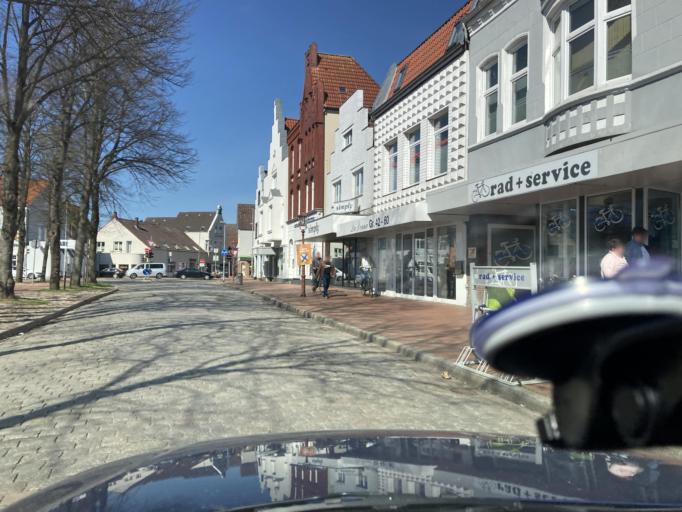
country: DE
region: Schleswig-Holstein
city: Heide
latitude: 54.1951
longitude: 9.0946
